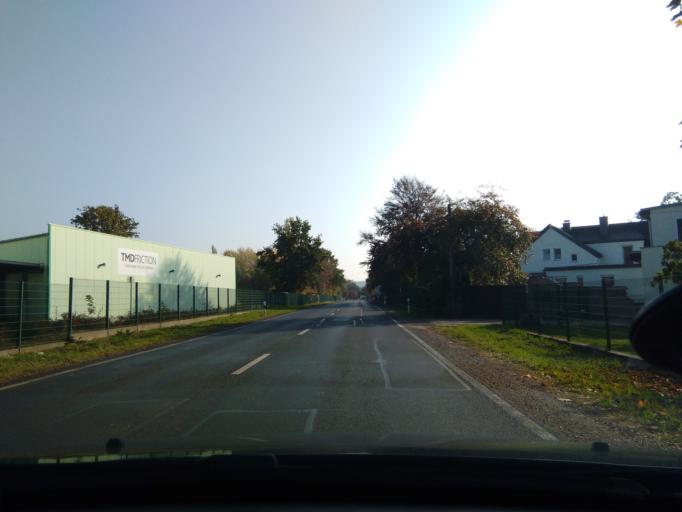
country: DE
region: Saxony
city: Coswig
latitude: 51.1270
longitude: 13.5665
